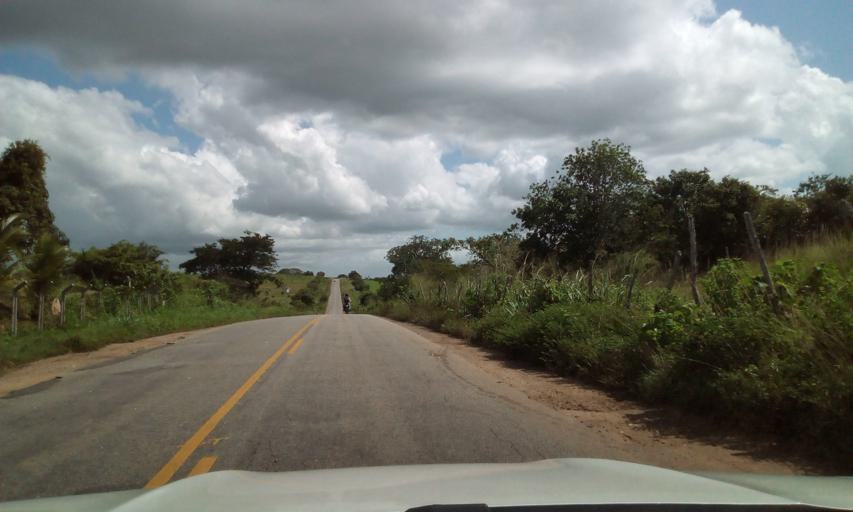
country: BR
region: Paraiba
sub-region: Guarabira
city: Guarabira
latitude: -6.8554
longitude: -35.4085
